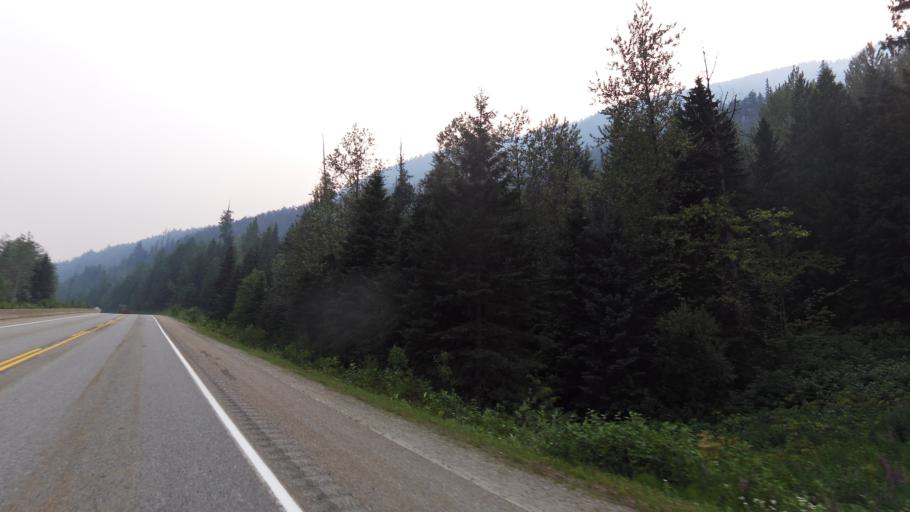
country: CA
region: Alberta
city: Jasper Park Lodge
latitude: 52.3086
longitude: -119.1817
